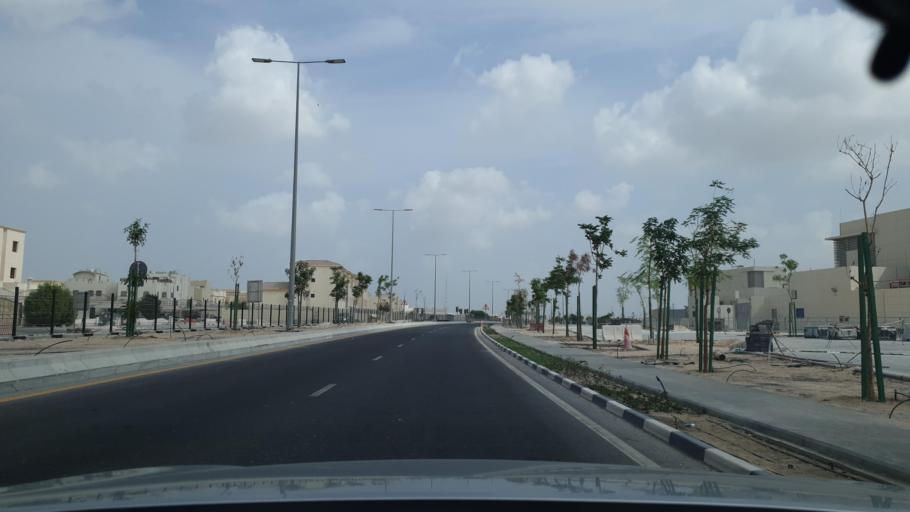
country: QA
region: Baladiyat ar Rayyan
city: Ar Rayyan
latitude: 25.2757
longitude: 51.4454
